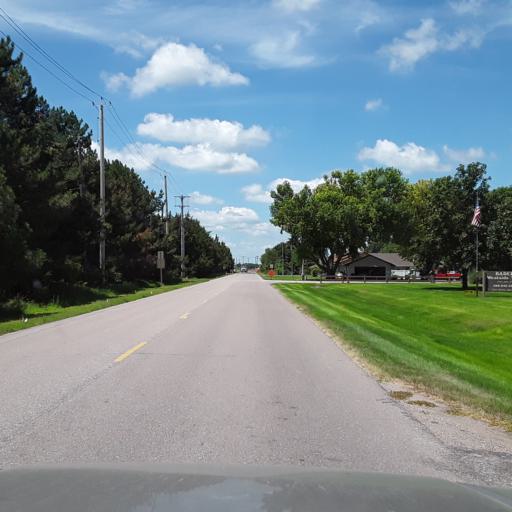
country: US
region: Nebraska
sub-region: Merrick County
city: Central City
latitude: 41.1048
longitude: -98.0139
